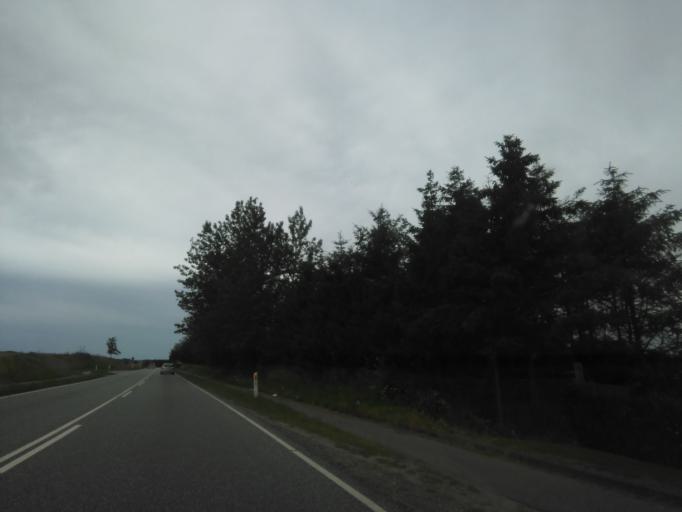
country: DK
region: Central Jutland
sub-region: Skanderborg Kommune
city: Skanderborg
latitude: 55.9364
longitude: 9.9557
